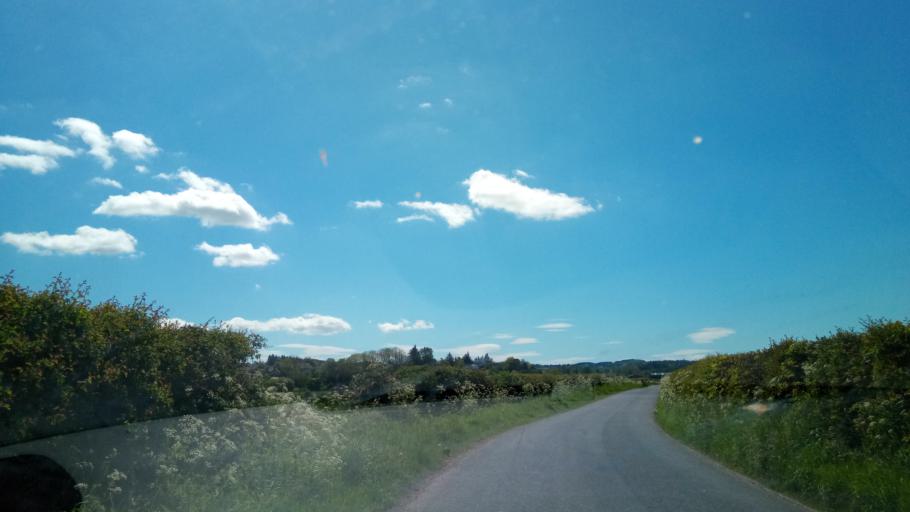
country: GB
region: Scotland
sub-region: The Scottish Borders
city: Hawick
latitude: 55.4649
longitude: -2.6807
